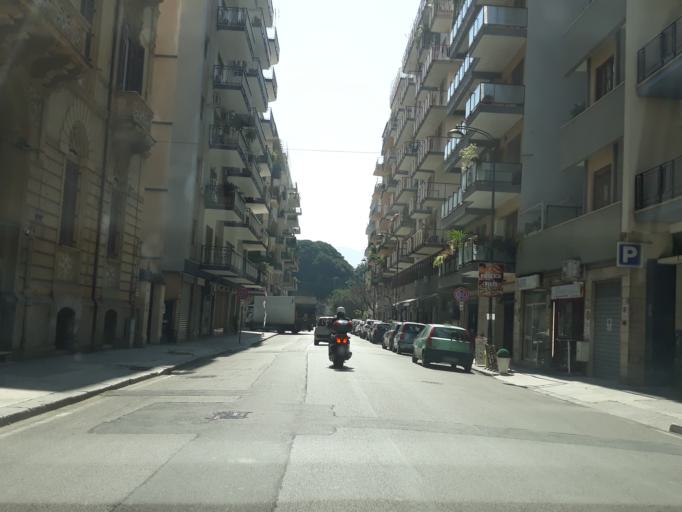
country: IT
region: Sicily
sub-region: Palermo
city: Palermo
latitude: 38.1354
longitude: 13.3505
